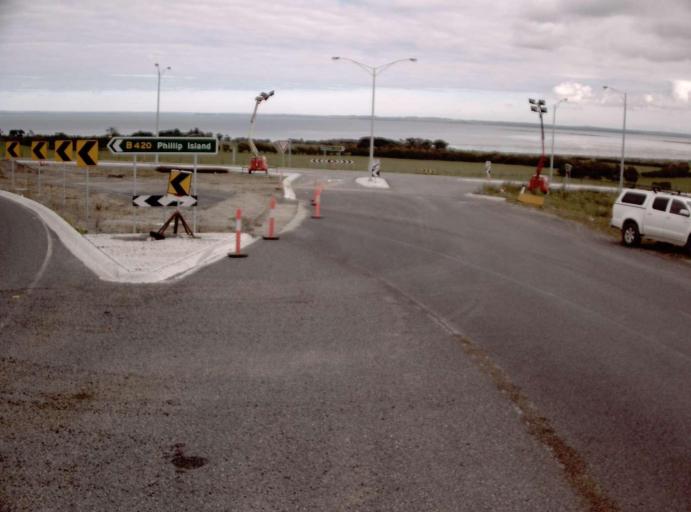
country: AU
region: Victoria
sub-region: Bass Coast
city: North Wonthaggi
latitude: -38.5223
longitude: 145.4315
